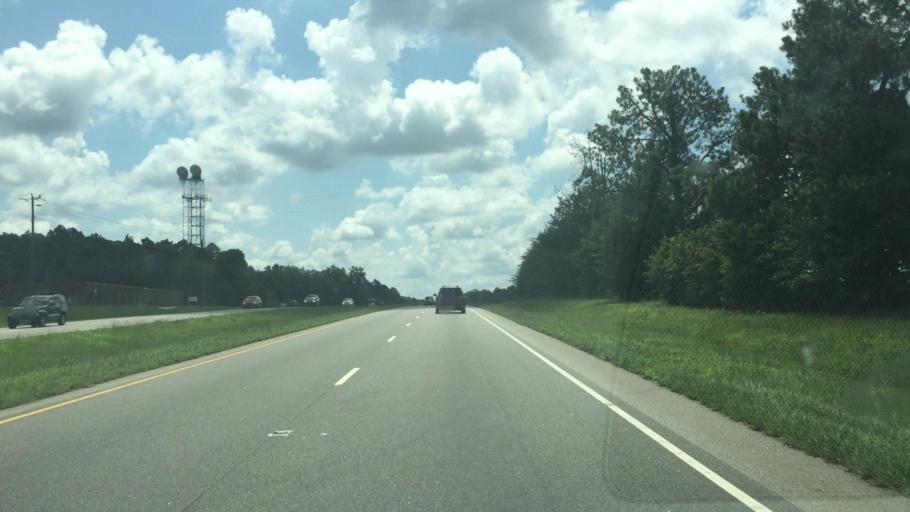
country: US
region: North Carolina
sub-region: Scotland County
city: Laurel Hill
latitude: 34.7957
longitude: -79.5161
